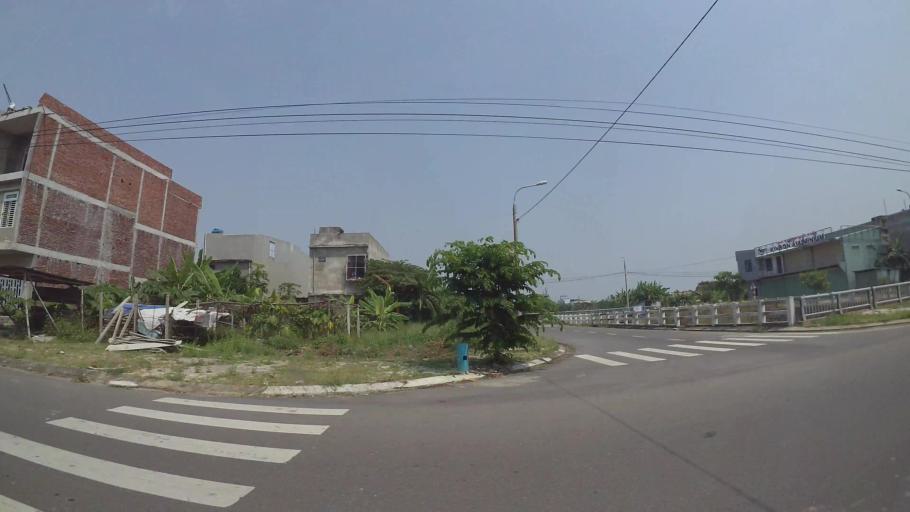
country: VN
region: Da Nang
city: Cam Le
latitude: 15.9902
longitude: 108.2109
